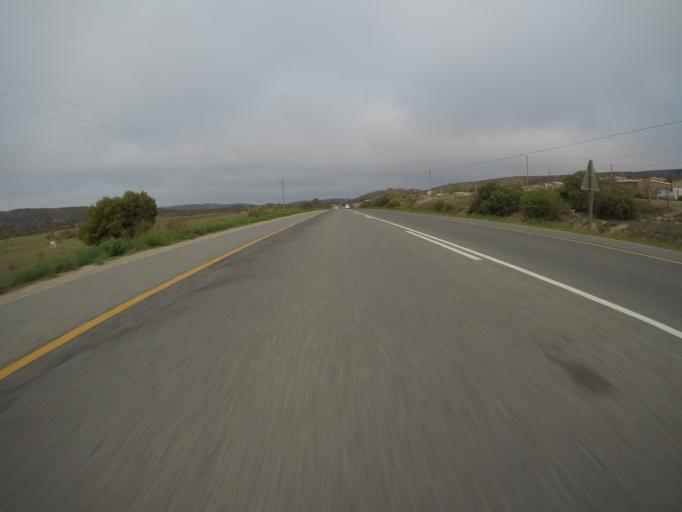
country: ZA
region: Western Cape
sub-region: Eden District Municipality
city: Mossel Bay
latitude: -34.1144
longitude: 22.0849
